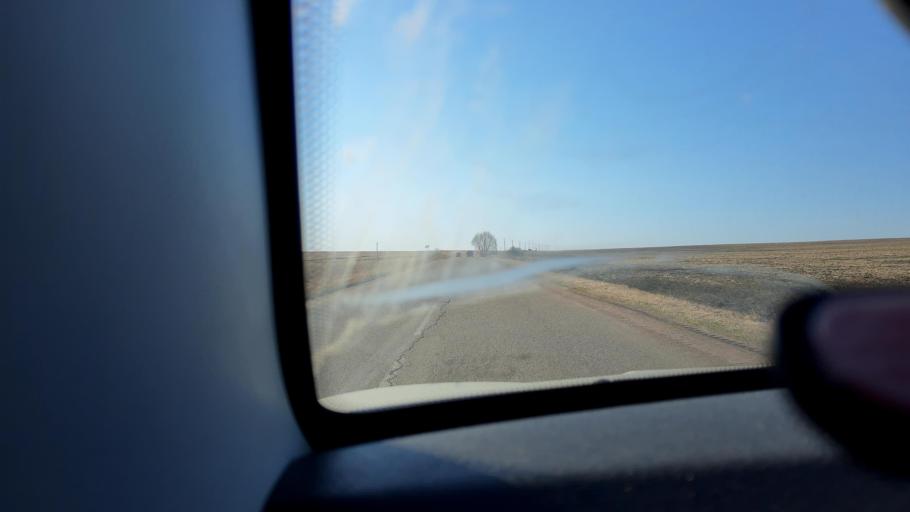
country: RU
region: Bashkortostan
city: Asanovo
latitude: 54.7996
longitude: 55.4969
